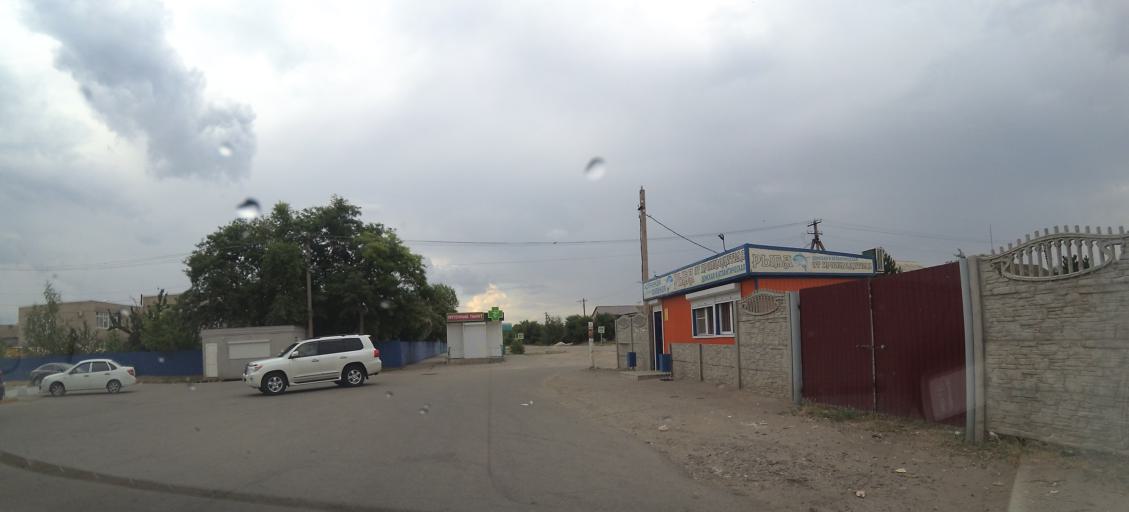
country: RU
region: Volgograd
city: Kotel'nikovo
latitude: 47.6372
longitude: 43.1213
